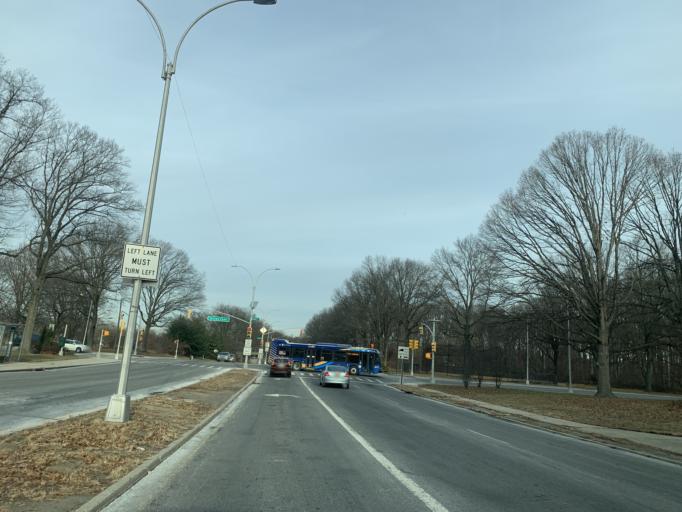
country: US
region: New York
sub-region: Nassau County
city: Bellerose Terrace
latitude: 40.7313
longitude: -73.7696
